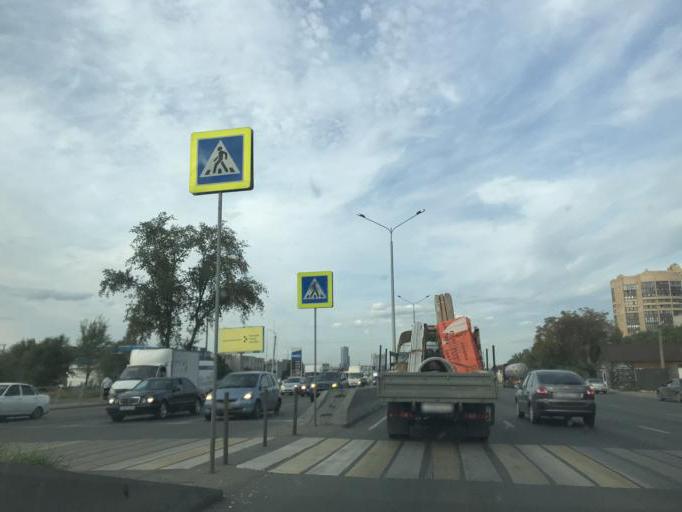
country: RU
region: Chelyabinsk
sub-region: Gorod Chelyabinsk
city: Chelyabinsk
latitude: 55.1449
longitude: 61.4253
